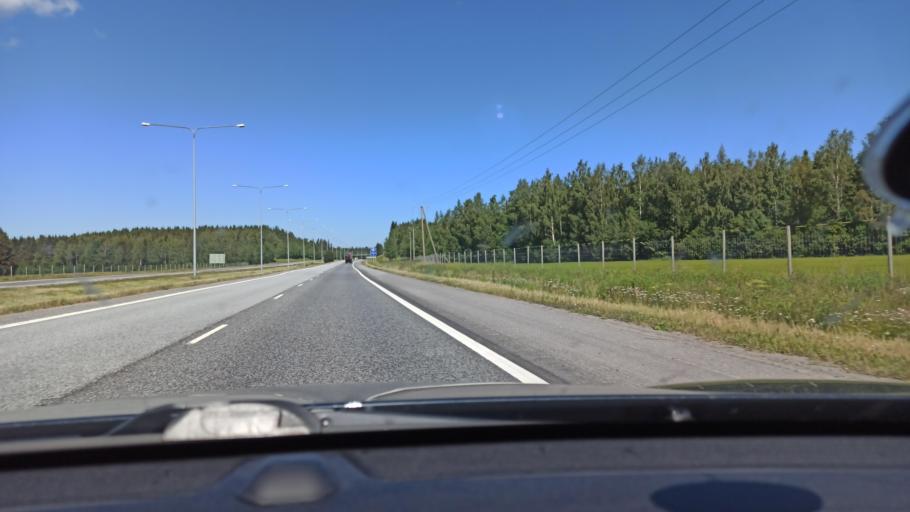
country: FI
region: Ostrobothnia
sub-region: Vaasa
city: Ristinummi
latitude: 63.0465
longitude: 21.7229
